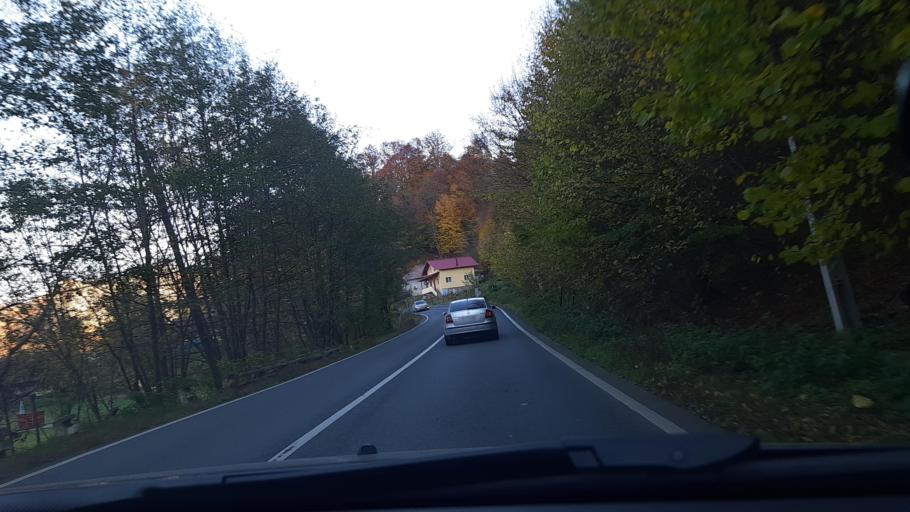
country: RO
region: Valcea
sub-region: Comuna Brezoi
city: Brezoi
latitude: 45.3436
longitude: 24.2255
